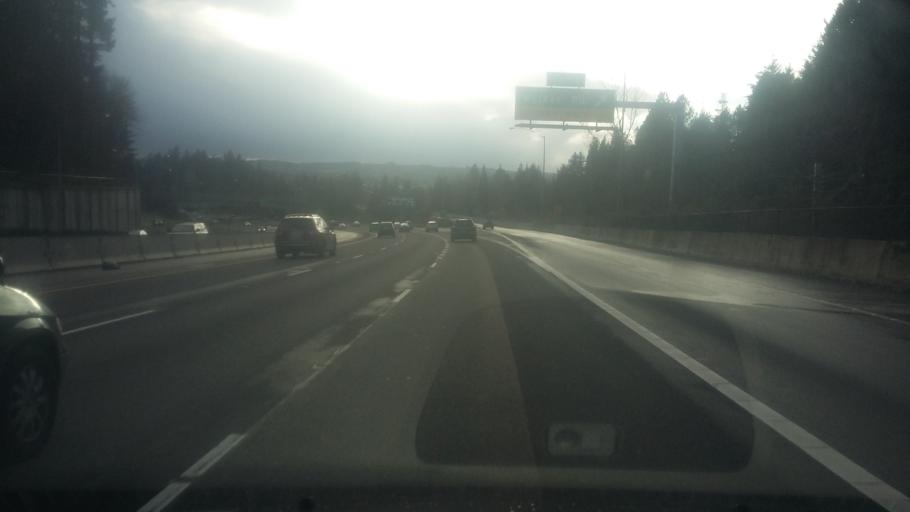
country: US
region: Oregon
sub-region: Washington County
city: Cedar Hills
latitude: 45.5016
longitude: -122.7878
